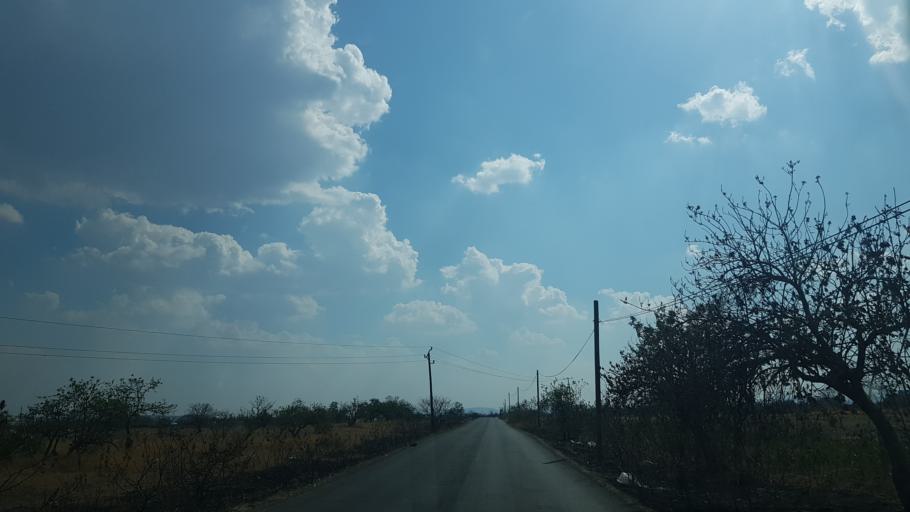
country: MX
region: Puebla
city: Atlixco
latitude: 18.9054
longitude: -98.4818
